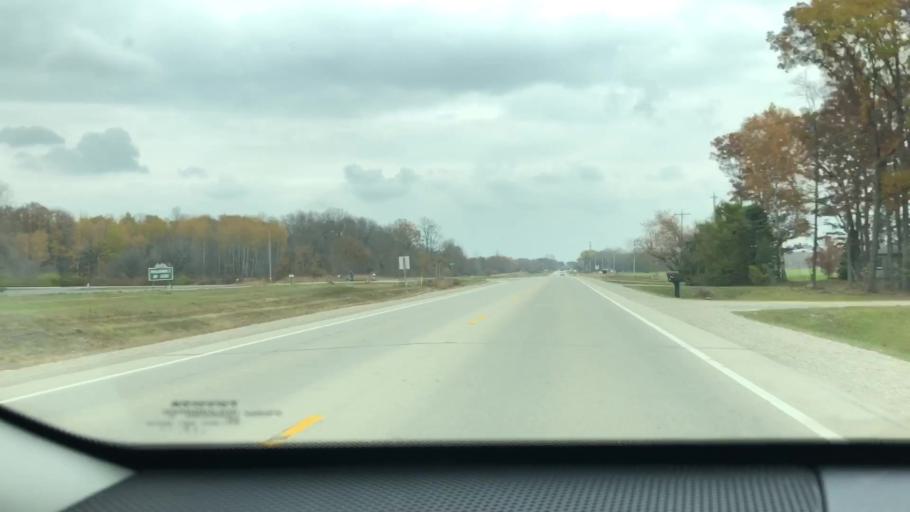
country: US
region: Wisconsin
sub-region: Brown County
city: Oneida
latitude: 44.5020
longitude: -88.2120
